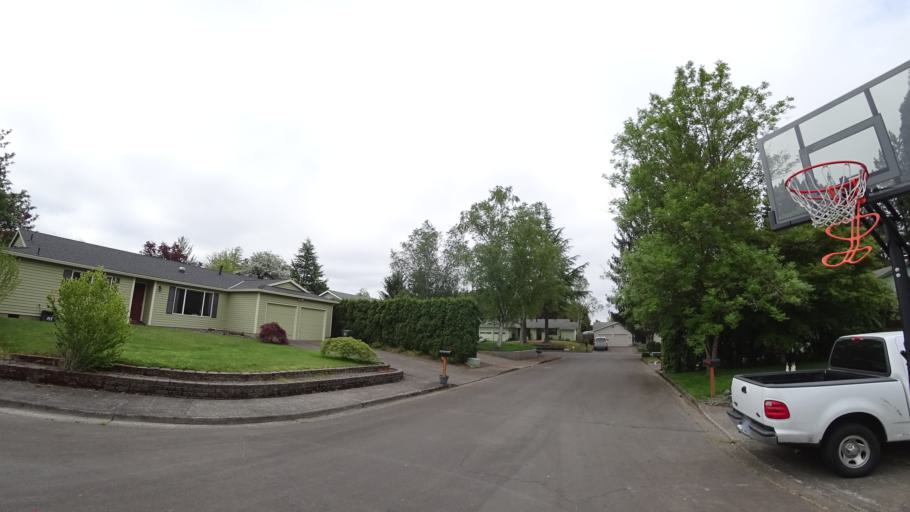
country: US
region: Oregon
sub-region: Washington County
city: Aloha
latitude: 45.5153
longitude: -122.8773
